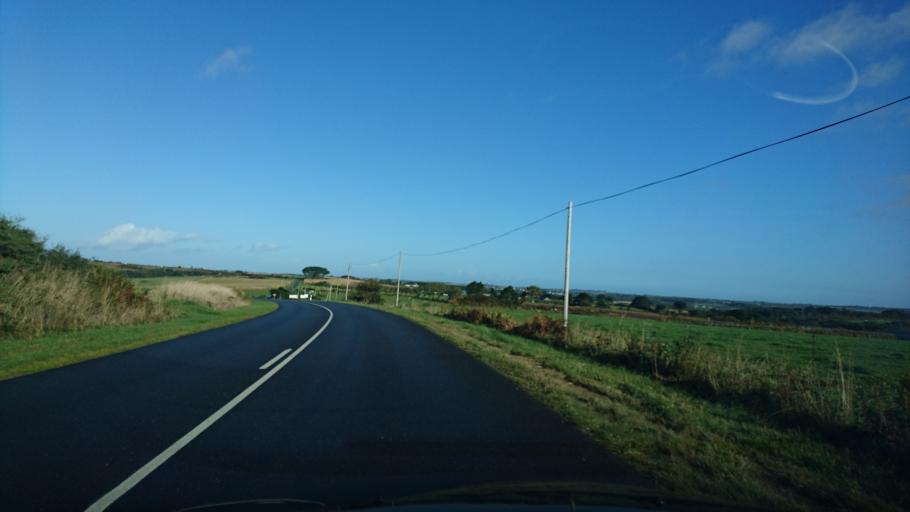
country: FR
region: Brittany
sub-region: Departement du Finistere
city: Plouarzel
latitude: 48.4363
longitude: -4.7157
